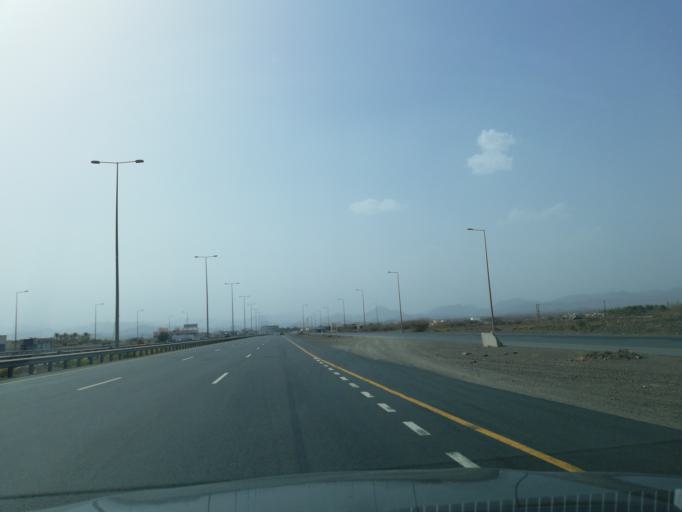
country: OM
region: Muhafazat ad Dakhiliyah
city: Sufalat Sama'il
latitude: 23.0209
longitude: 58.2150
